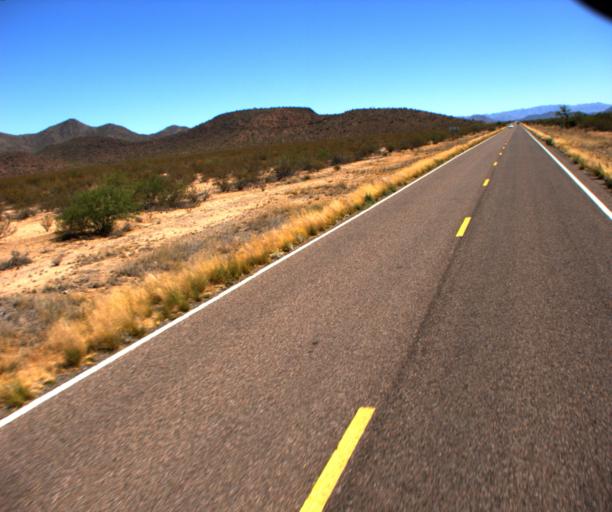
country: US
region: Arizona
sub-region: Yavapai County
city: Congress
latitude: 34.0014
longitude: -113.1199
